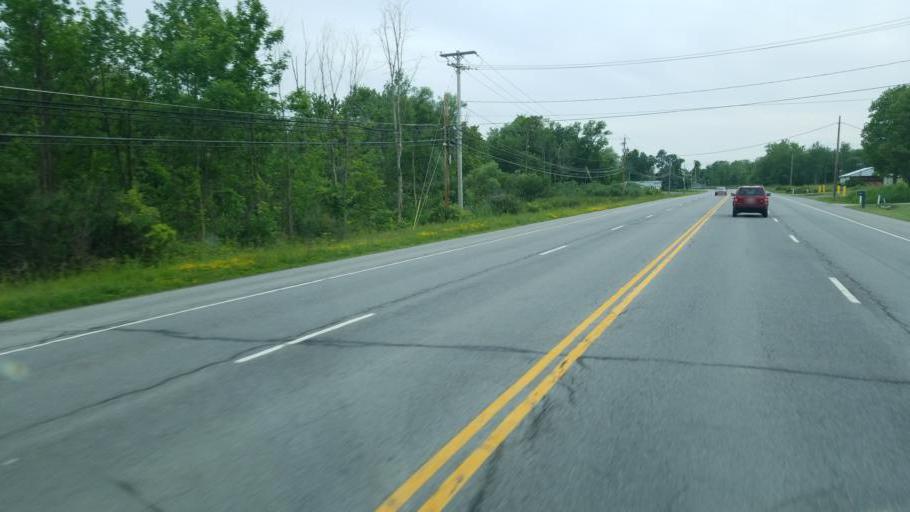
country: US
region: New York
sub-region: Genesee County
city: Batavia
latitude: 43.0066
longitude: -78.2419
